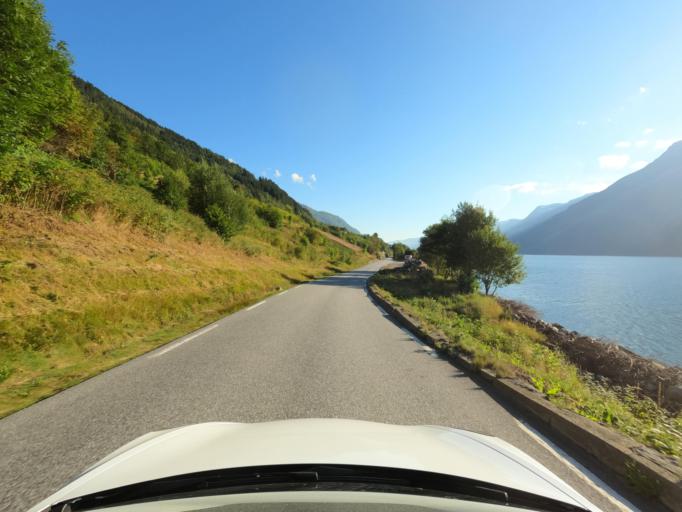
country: NO
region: Hordaland
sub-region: Ullensvang
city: Kinsarvik
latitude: 60.3481
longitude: 6.6607
